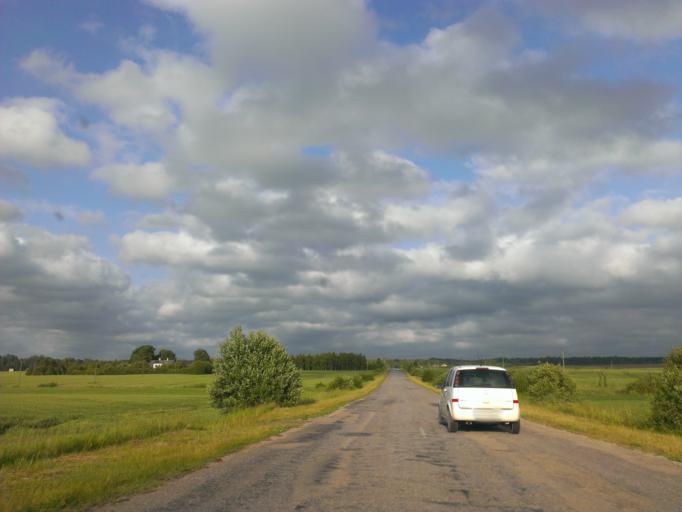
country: LV
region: Aizpute
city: Aizpute
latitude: 56.7330
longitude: 21.6997
